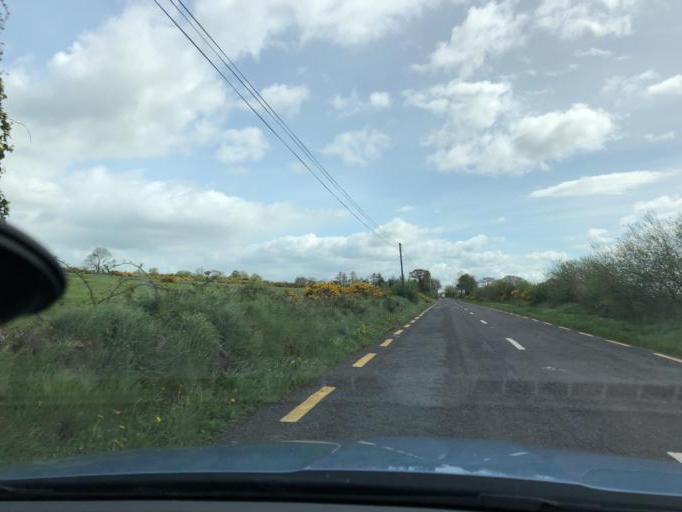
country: IE
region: Munster
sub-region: County Cork
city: Millstreet
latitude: 52.0865
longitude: -9.1608
